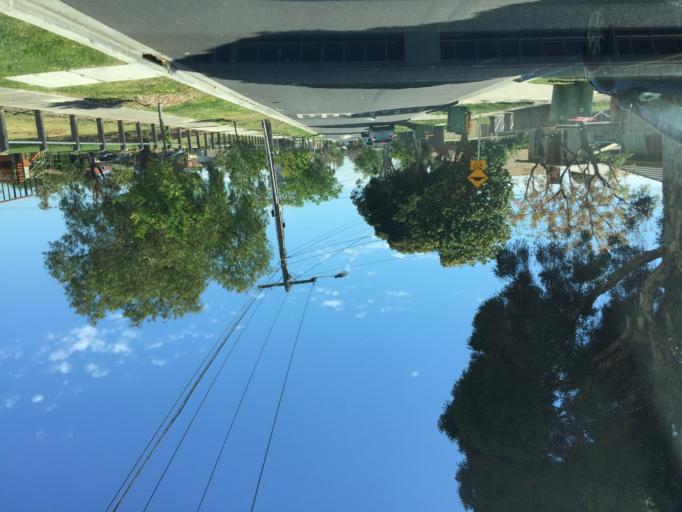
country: AU
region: Victoria
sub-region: Maribyrnong
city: Braybrook
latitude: -37.7834
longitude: 144.8501
